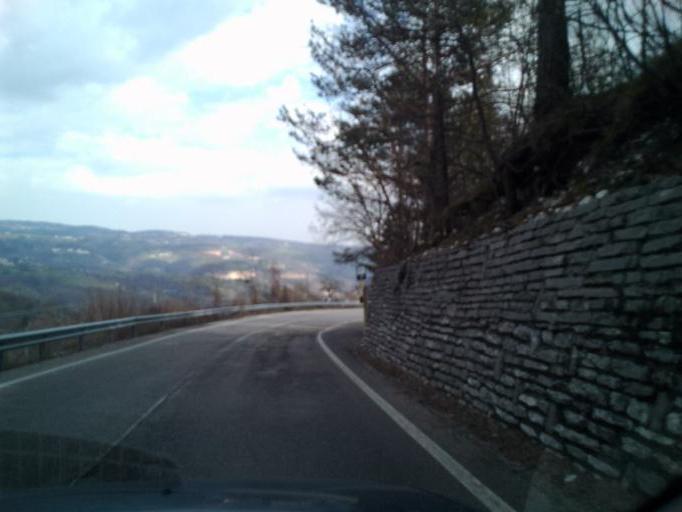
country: IT
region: Veneto
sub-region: Provincia di Verona
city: Sant'Anna d'Alfaedo
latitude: 45.6115
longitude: 10.9495
